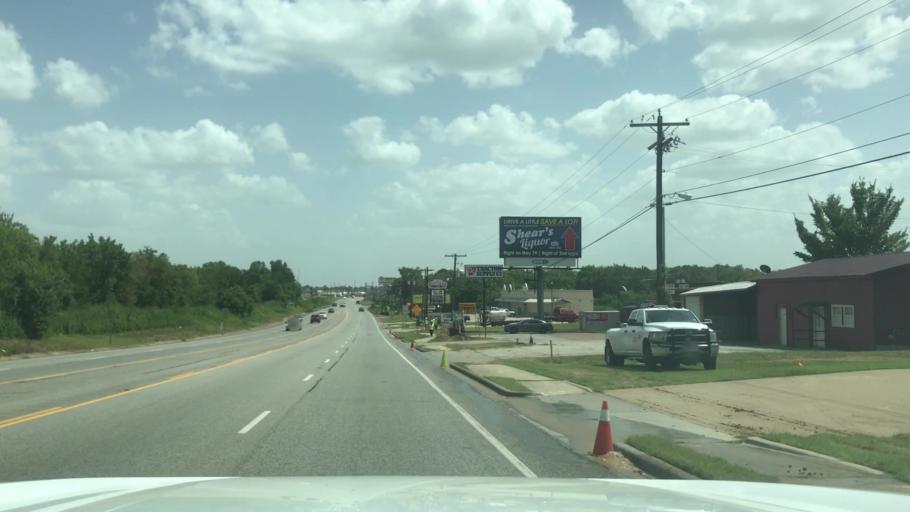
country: US
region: Texas
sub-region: Robertson County
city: Hearne
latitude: 30.8918
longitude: -96.6000
